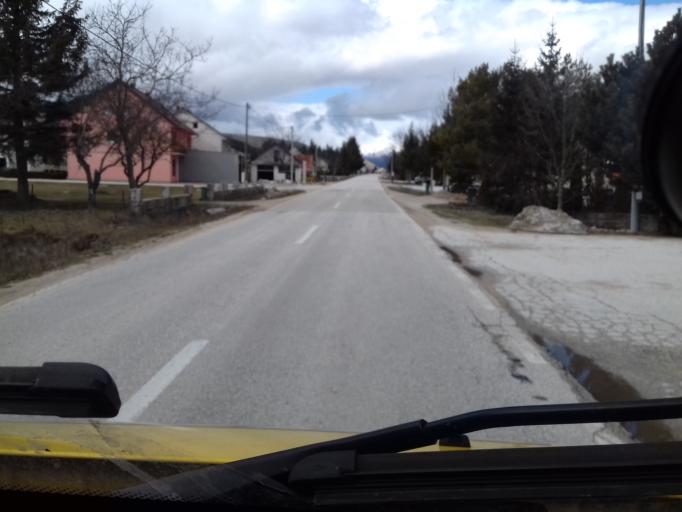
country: BA
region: Federation of Bosnia and Herzegovina
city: Tomislavgrad
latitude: 43.6272
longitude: 17.2511
